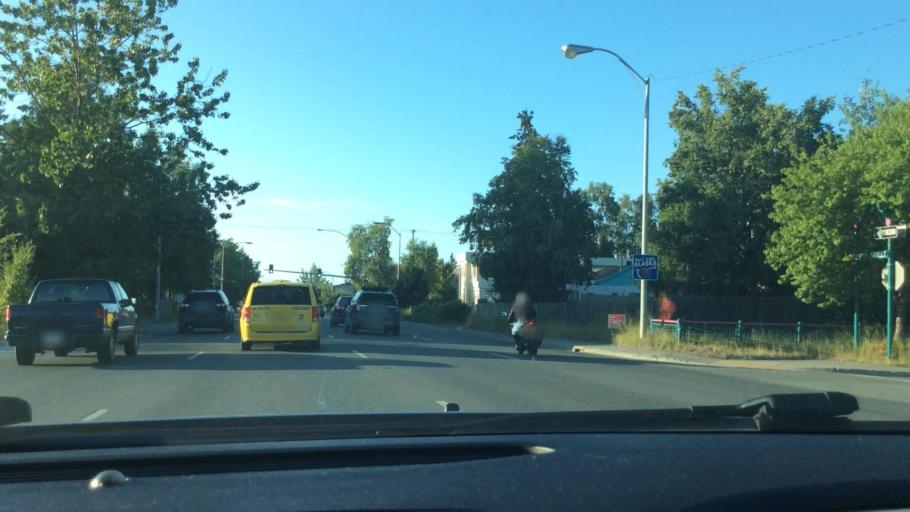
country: US
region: Alaska
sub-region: Anchorage Municipality
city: Anchorage
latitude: 61.2086
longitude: -149.8670
